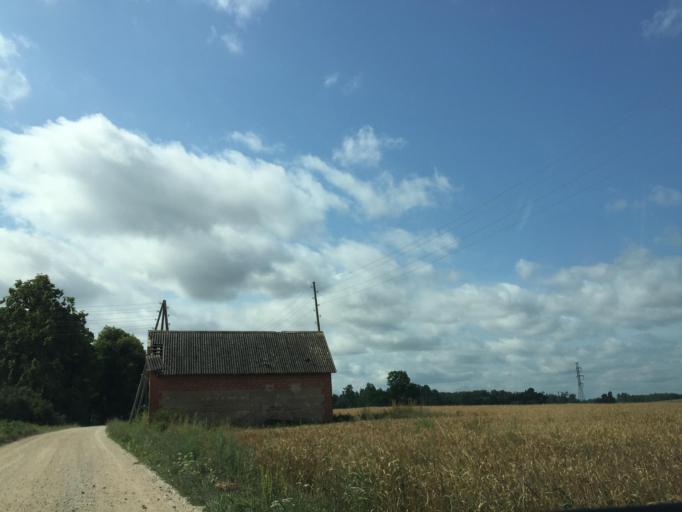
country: LV
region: Kandava
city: Kandava
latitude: 56.9745
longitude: 22.9291
